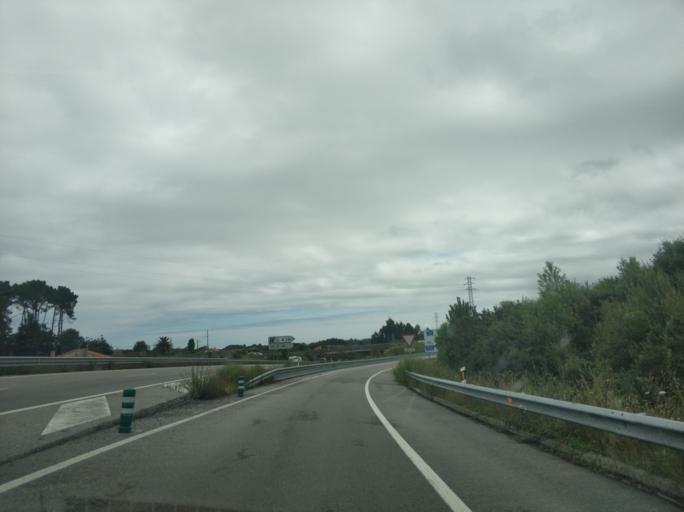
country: ES
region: Asturias
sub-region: Province of Asturias
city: Cudillero
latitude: 43.5646
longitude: -6.2447
